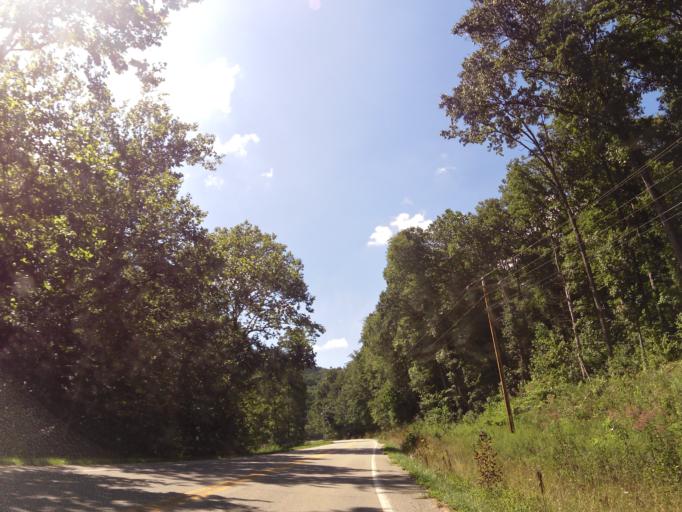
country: US
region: Tennessee
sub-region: Cumberland County
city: Fairfield Glade
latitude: 35.8860
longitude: -84.8365
